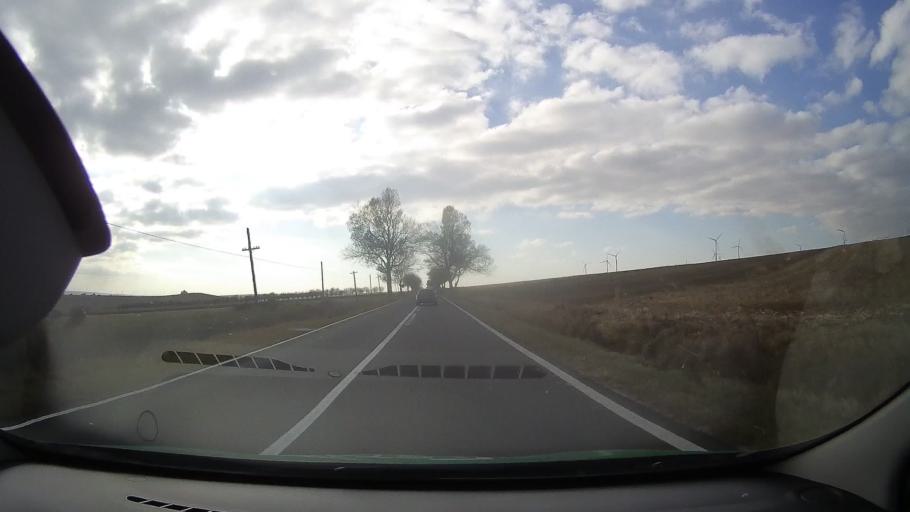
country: RO
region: Tulcea
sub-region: Comuna Topolog
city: Topolog
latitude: 44.8882
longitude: 28.3908
